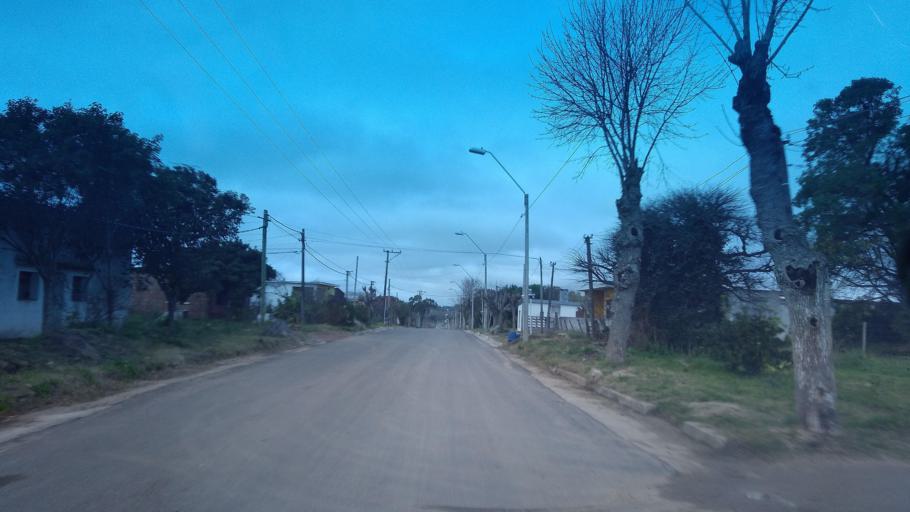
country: UY
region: Canelones
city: Tala
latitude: -34.1995
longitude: -55.7406
